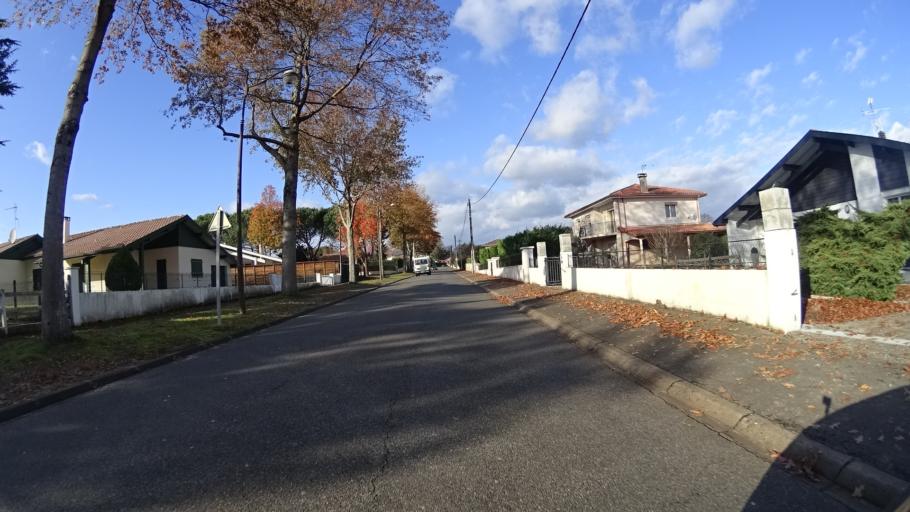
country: FR
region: Aquitaine
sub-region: Departement des Landes
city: Saint-Paul-les-Dax
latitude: 43.7232
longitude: -1.0830
